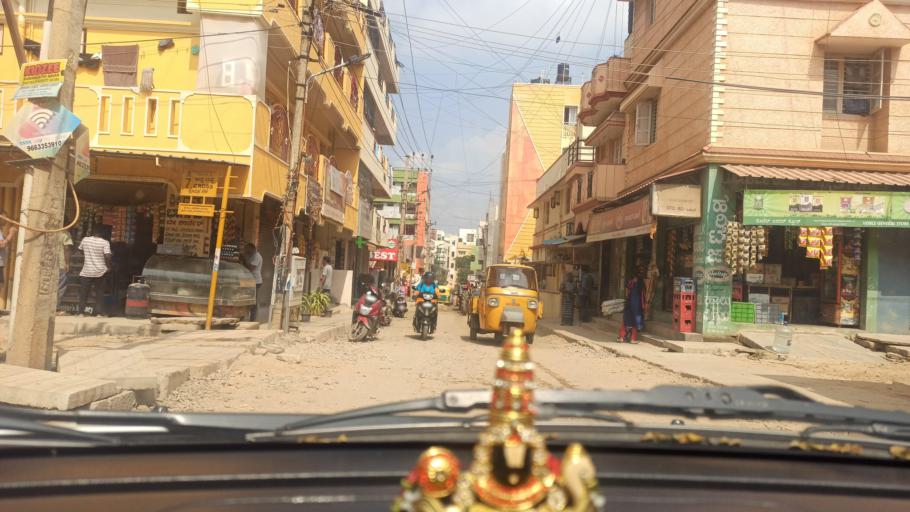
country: IN
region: Karnataka
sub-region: Bangalore Urban
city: Bangalore
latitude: 13.0169
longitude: 77.6653
